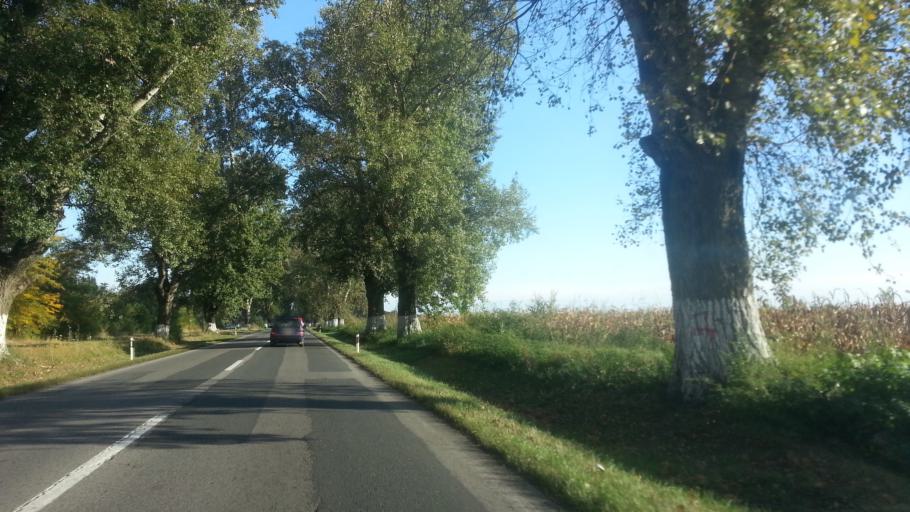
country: RS
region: Autonomna Pokrajina Vojvodina
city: Nova Pazova
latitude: 44.9288
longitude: 20.2419
